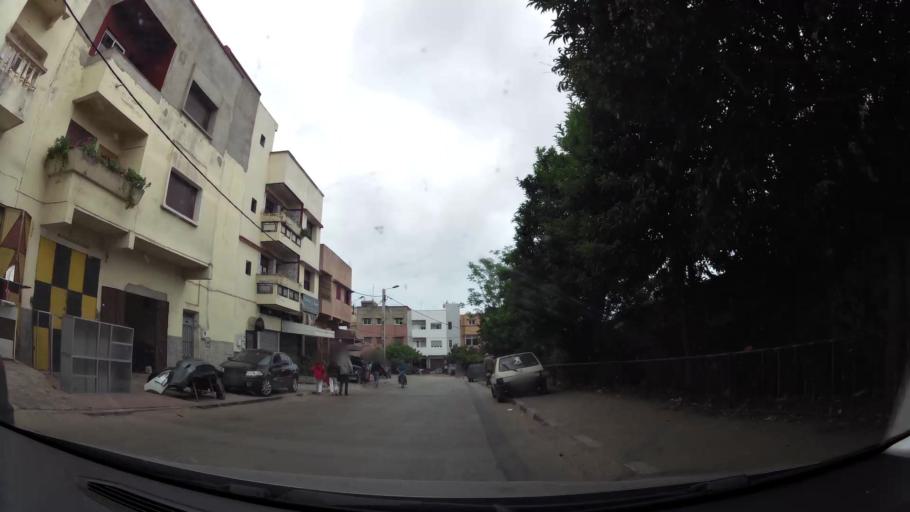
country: MA
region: Rabat-Sale-Zemmour-Zaer
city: Sale
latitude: 34.0414
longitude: -6.8019
